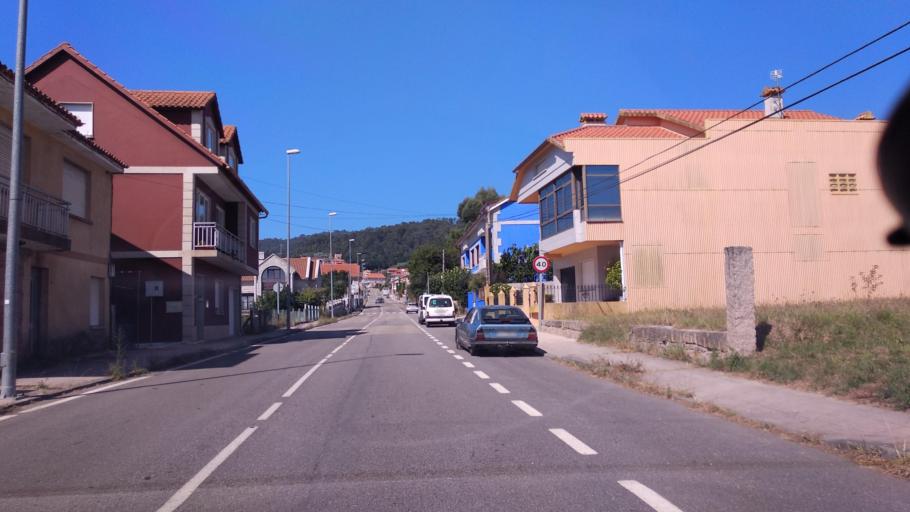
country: ES
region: Galicia
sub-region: Provincia de Pontevedra
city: Cangas
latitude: 42.2716
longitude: -8.7676
